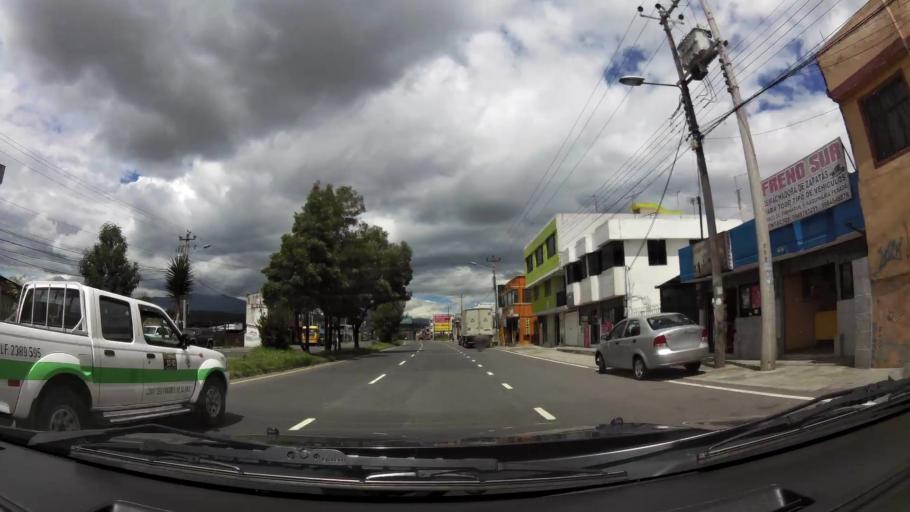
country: EC
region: Pichincha
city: Sangolqui
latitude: -0.3526
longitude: -78.5496
